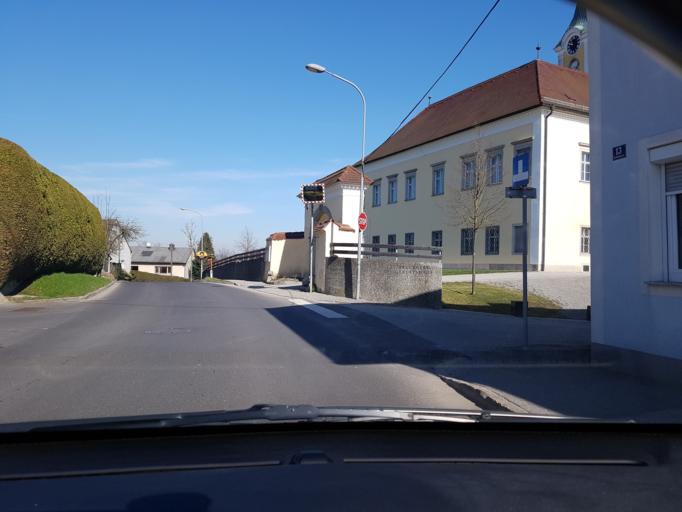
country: AT
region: Upper Austria
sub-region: Politischer Bezirk Linz-Land
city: Ansfelden
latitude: 48.2087
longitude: 14.2902
